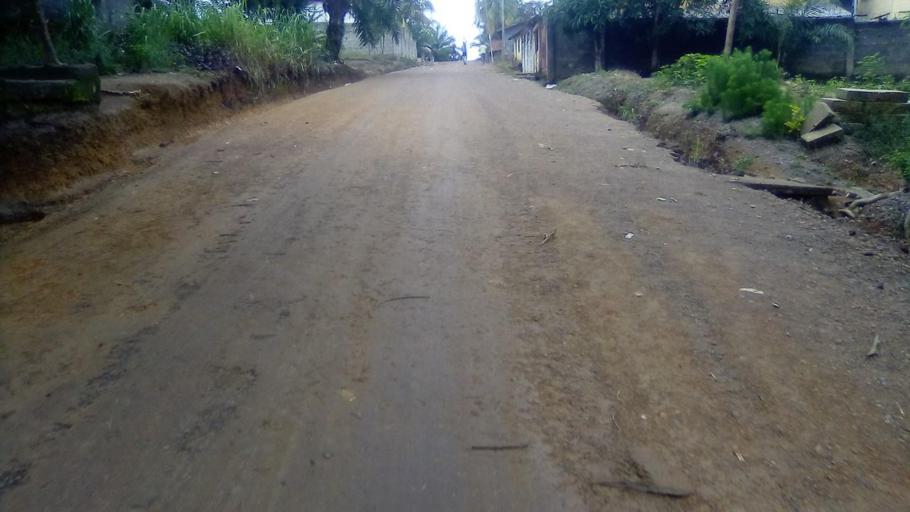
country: SL
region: Southern Province
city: Bo
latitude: 7.9426
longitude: -11.7427
